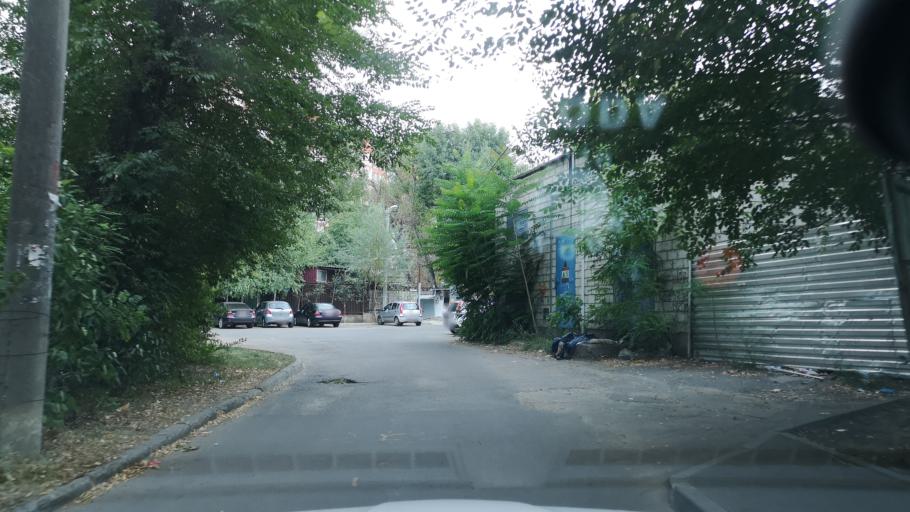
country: MD
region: Chisinau
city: Chisinau
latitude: 46.9976
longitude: 28.8526
